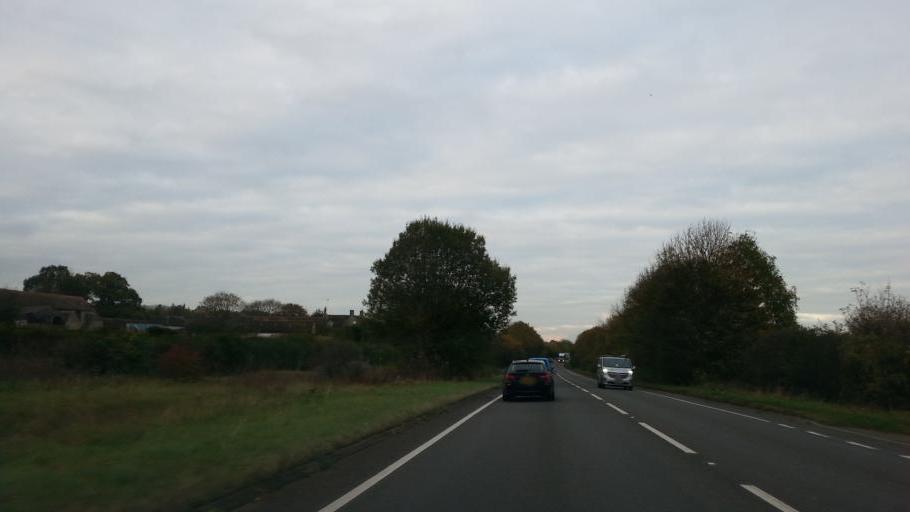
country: GB
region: England
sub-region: District of Rutland
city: South Luffenham
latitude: 52.5607
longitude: -0.5741
